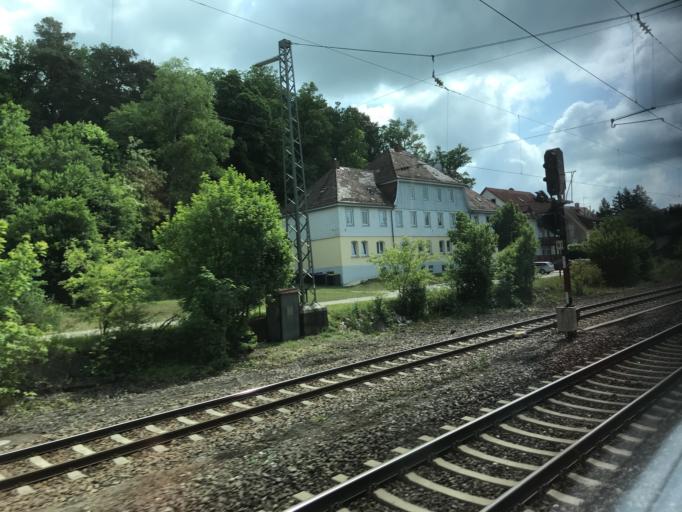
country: DE
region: Baden-Wuerttemberg
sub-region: Tuebingen Region
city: Westerstetten
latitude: 48.5242
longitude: 9.9451
